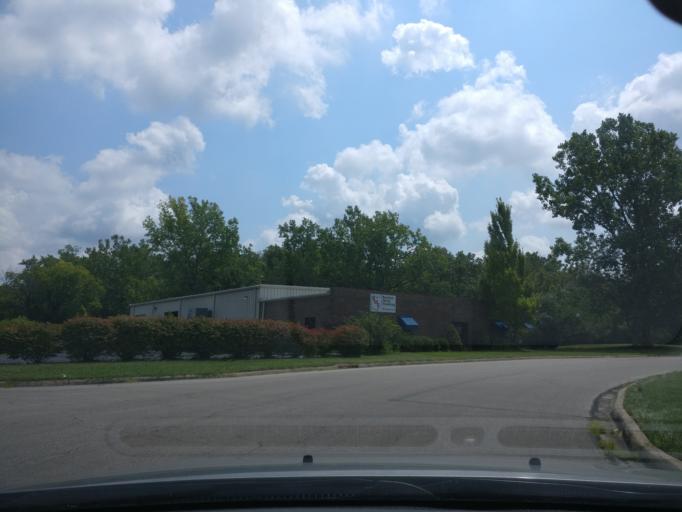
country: US
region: Ohio
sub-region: Montgomery County
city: West Carrollton City
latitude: 39.6569
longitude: -84.2378
